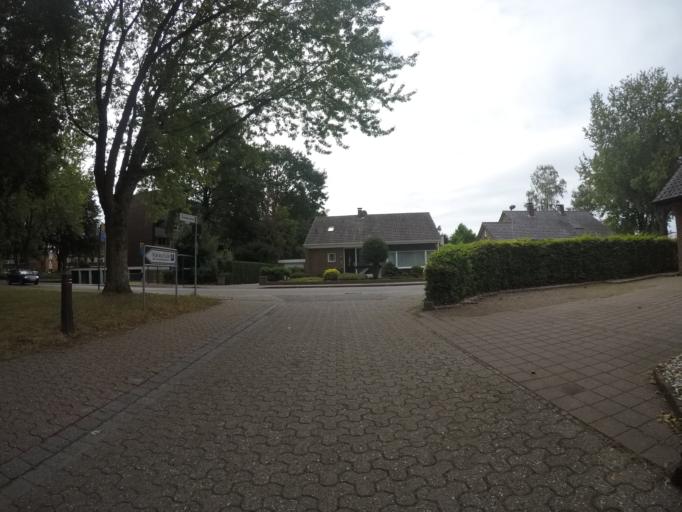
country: DE
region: North Rhine-Westphalia
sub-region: Regierungsbezirk Dusseldorf
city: Bocholt
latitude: 51.8429
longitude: 6.5915
